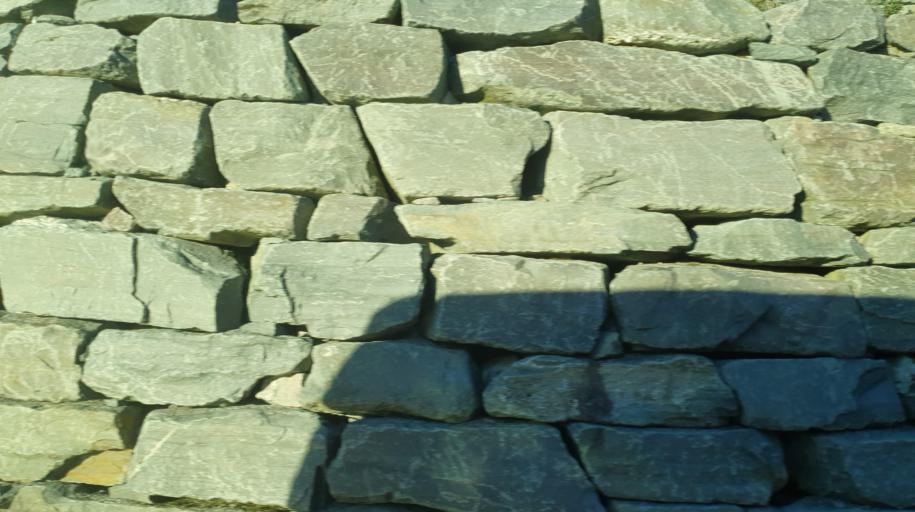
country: NO
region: Buskerud
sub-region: Krodsherad
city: Noresund
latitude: 60.2272
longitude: 9.5207
